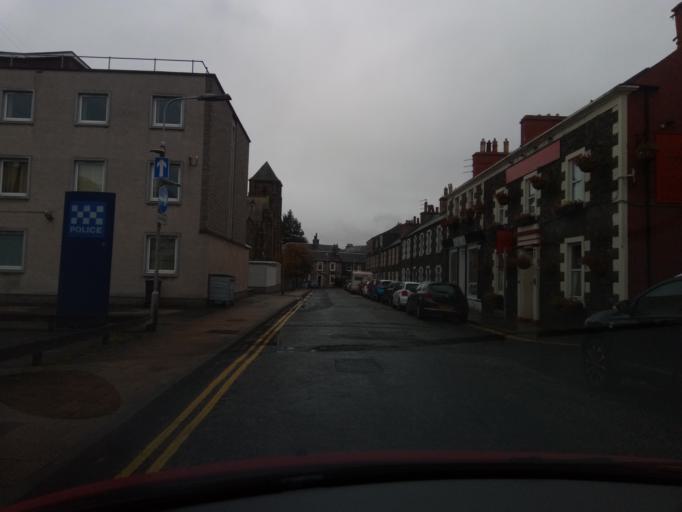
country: GB
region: Scotland
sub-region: The Scottish Borders
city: Galashiels
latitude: 55.6185
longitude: -2.8105
